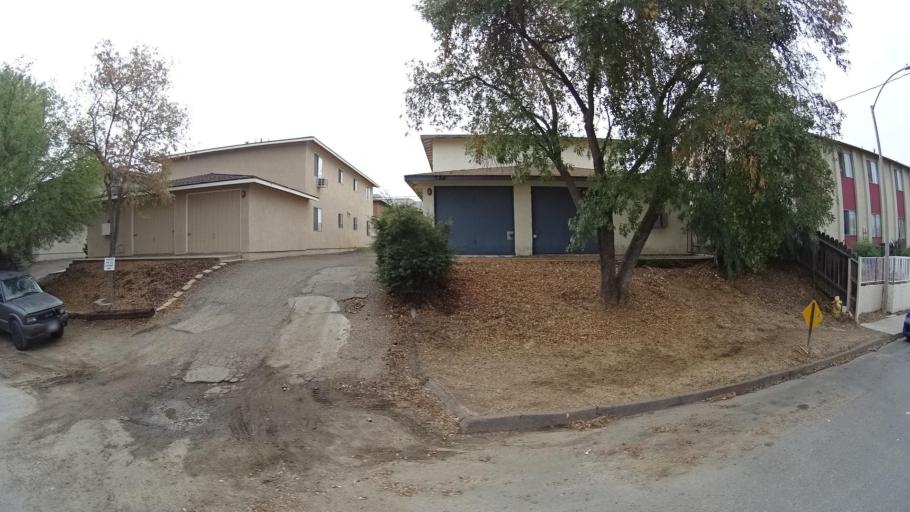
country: US
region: California
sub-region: San Diego County
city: Ramona
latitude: 33.0451
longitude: -116.8652
